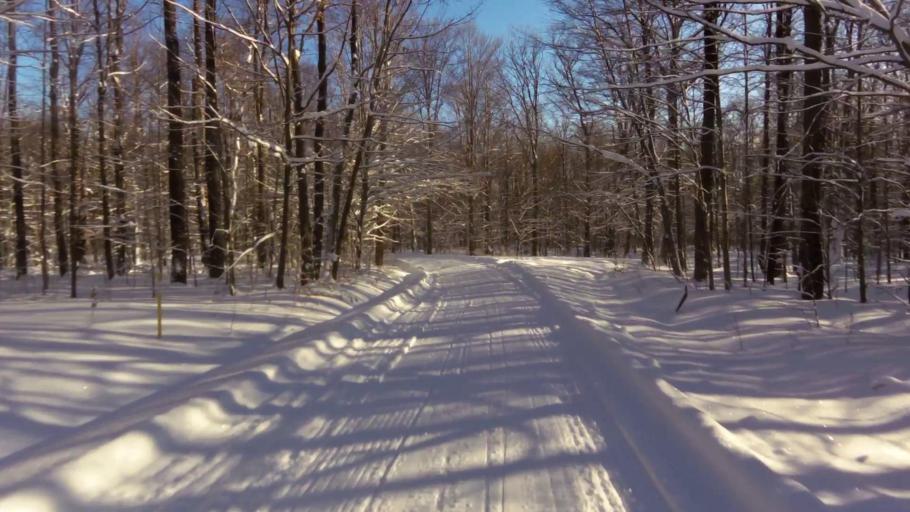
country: US
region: New York
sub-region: Chautauqua County
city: Falconer
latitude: 42.2501
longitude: -79.2118
